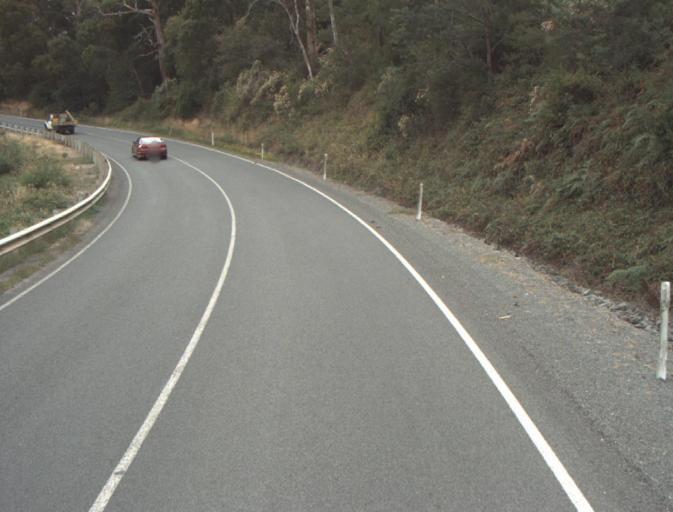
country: AU
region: Tasmania
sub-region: Launceston
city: Mayfield
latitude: -41.2283
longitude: 147.2090
